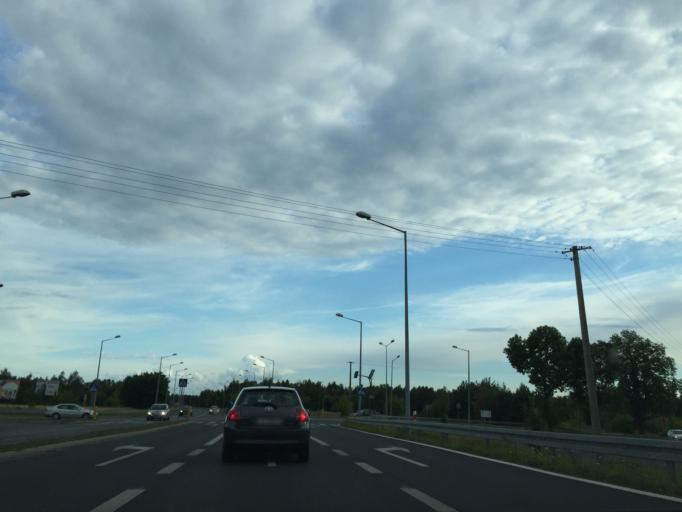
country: PL
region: Lublin Voivodeship
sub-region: Powiat lubartowski
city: Lubartow
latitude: 51.4636
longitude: 22.5769
